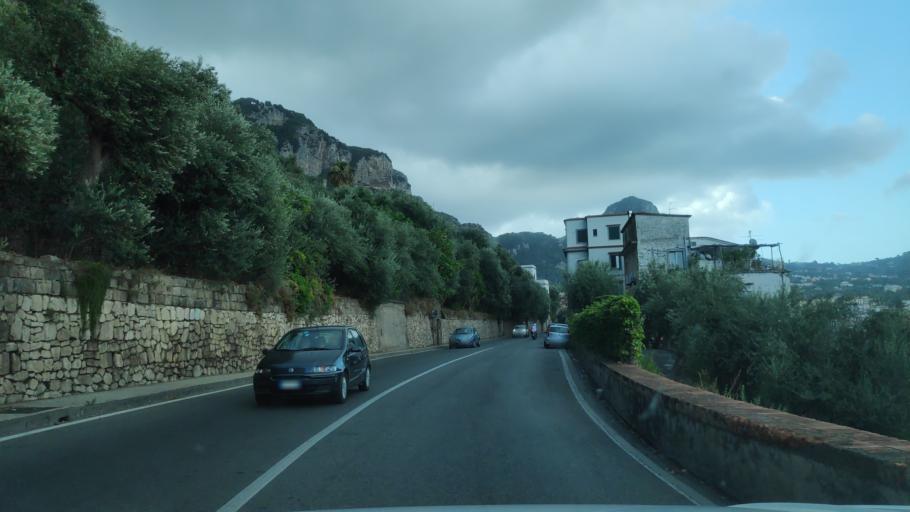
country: IT
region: Campania
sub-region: Provincia di Napoli
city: Meta
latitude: 40.6451
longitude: 14.4146
